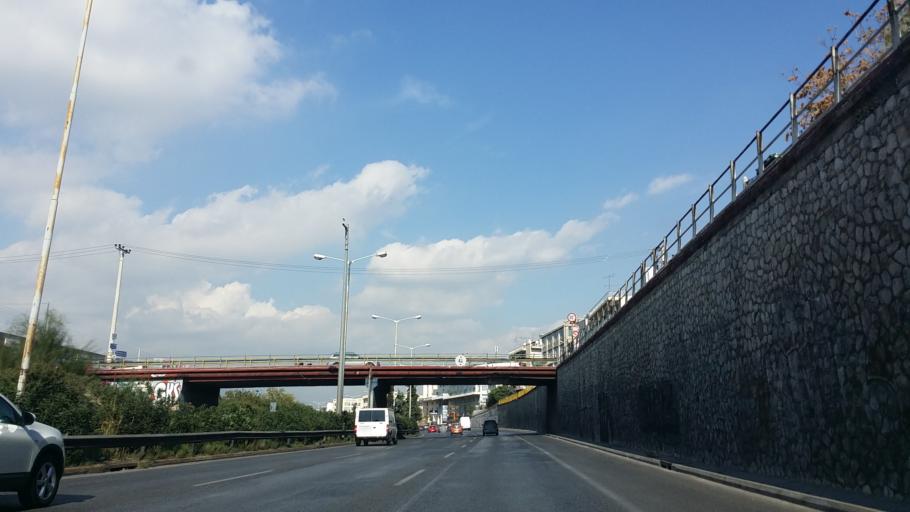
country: GR
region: Attica
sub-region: Nomarchia Athinas
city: Nea Filadelfeia
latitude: 38.0365
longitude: 23.7329
